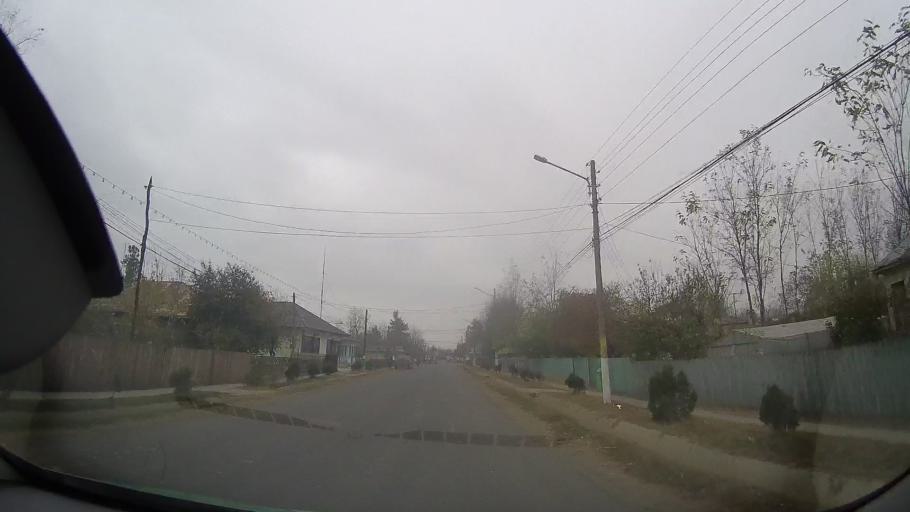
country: RO
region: Braila
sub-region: Comuna Ciocile
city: Ciocile
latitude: 44.8213
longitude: 27.2492
